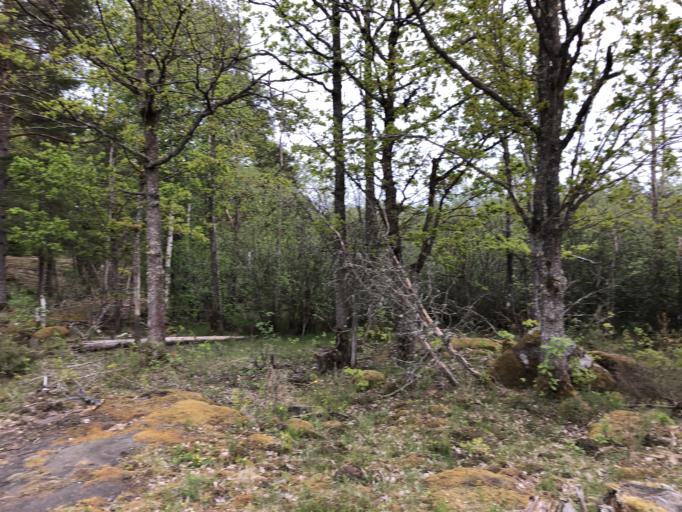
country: SE
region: Kalmar
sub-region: Oskarshamns Kommun
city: Oskarshamn
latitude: 57.4209
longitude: 16.2451
